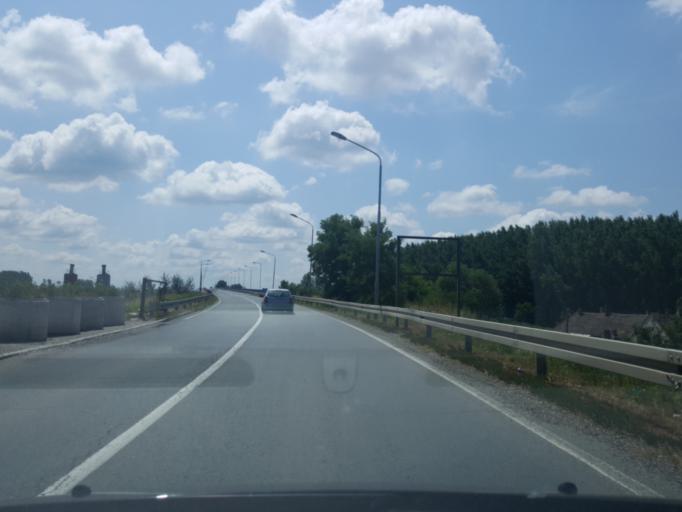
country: RS
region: Autonomna Pokrajina Vojvodina
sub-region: Sremski Okrug
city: Sremska Mitrovica
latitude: 44.9641
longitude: 19.6310
